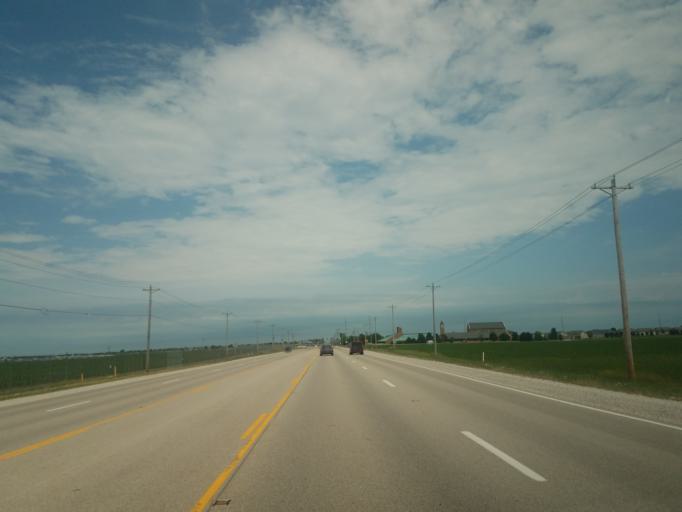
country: US
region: Illinois
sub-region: McLean County
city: Bloomington
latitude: 40.4843
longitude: -88.9024
